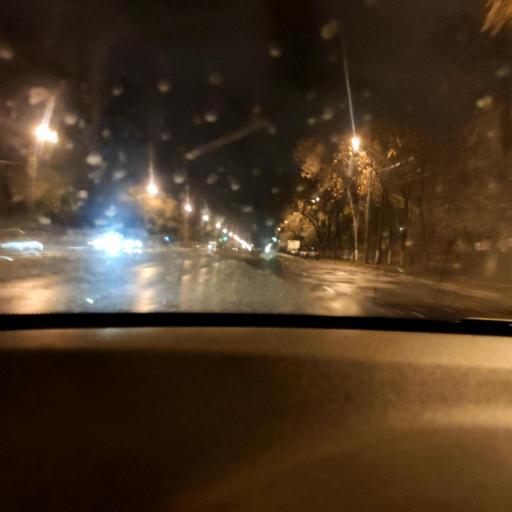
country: RU
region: Samara
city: Samara
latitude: 53.2014
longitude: 50.2131
